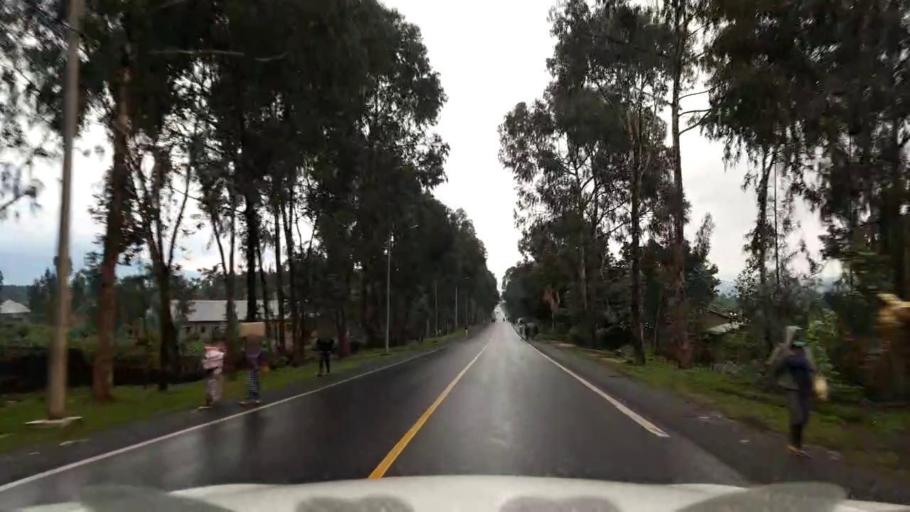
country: RW
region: Northern Province
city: Musanze
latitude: -1.5093
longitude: 29.5991
